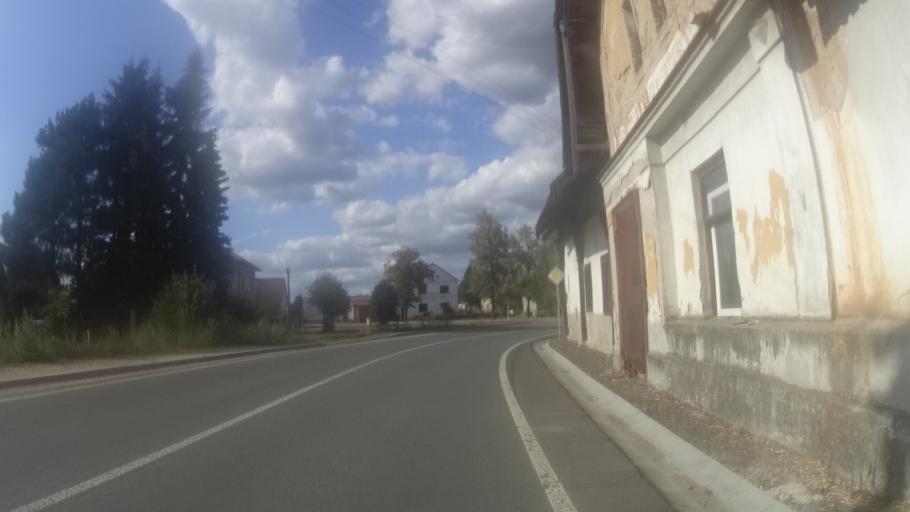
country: CZ
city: Albrechtice nad Orlici
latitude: 50.1189
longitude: 16.0688
